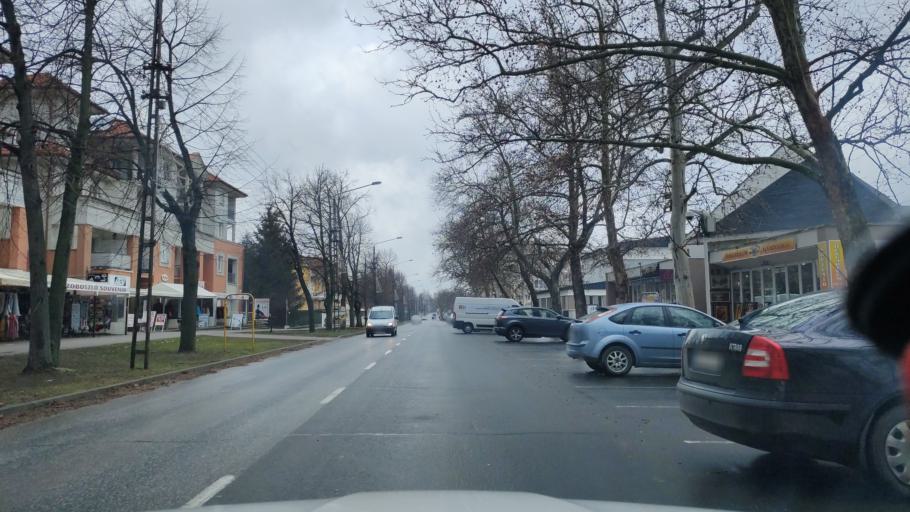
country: HU
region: Hajdu-Bihar
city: Hajduszoboszlo
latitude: 47.4491
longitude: 21.3989
